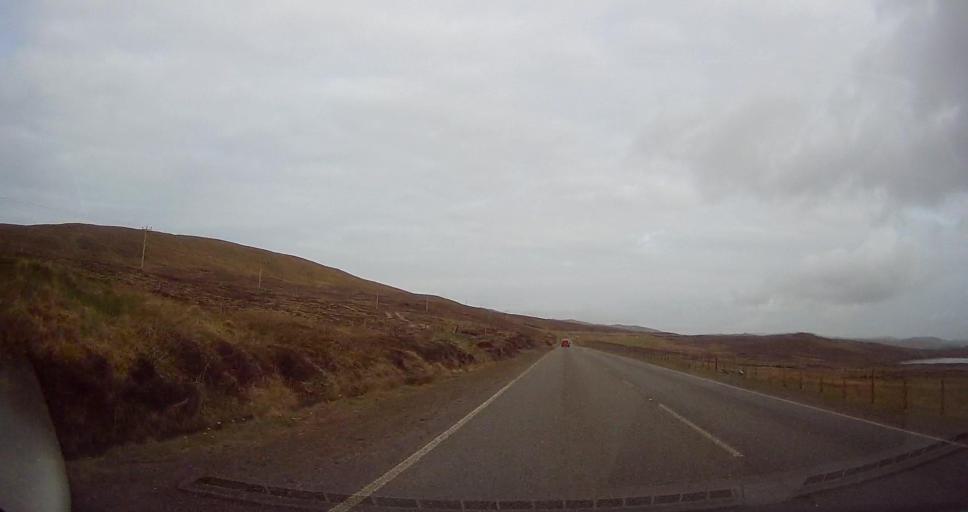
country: GB
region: Scotland
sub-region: Shetland Islands
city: Sandwick
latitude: 60.0787
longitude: -1.2294
